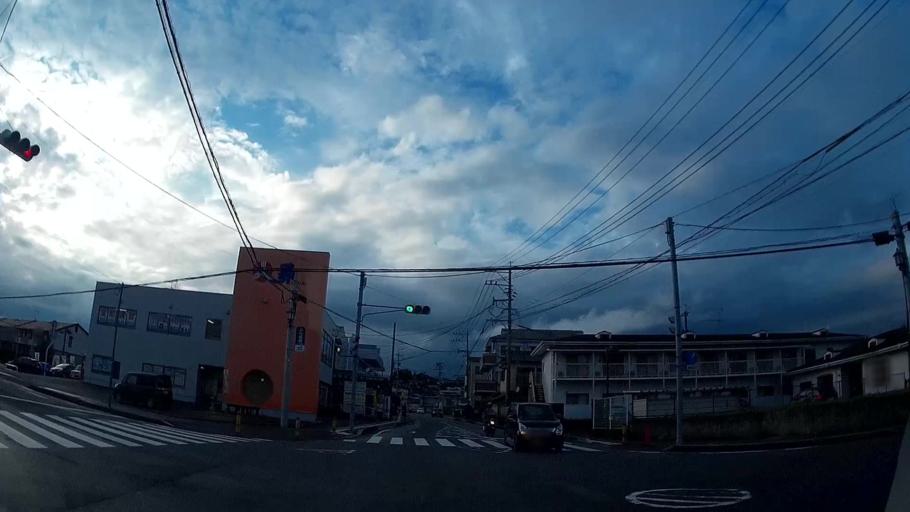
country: JP
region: Kumamoto
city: Ozu
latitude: 32.8763
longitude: 130.8701
